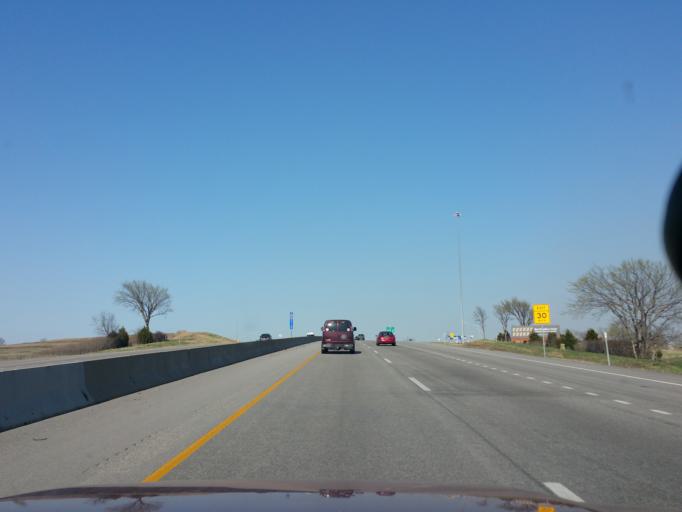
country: US
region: Kansas
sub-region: Leavenworth County
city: Tonganoxie
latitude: 39.0401
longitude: -95.1002
